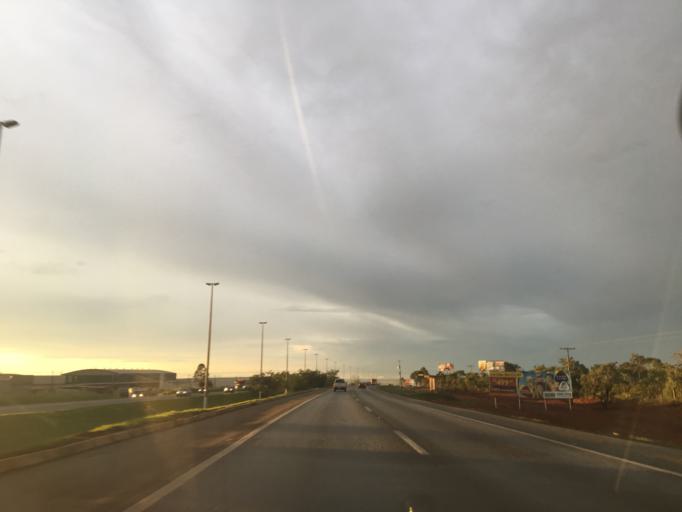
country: BR
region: Goias
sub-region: Luziania
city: Luziania
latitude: -16.0308
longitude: -47.9788
